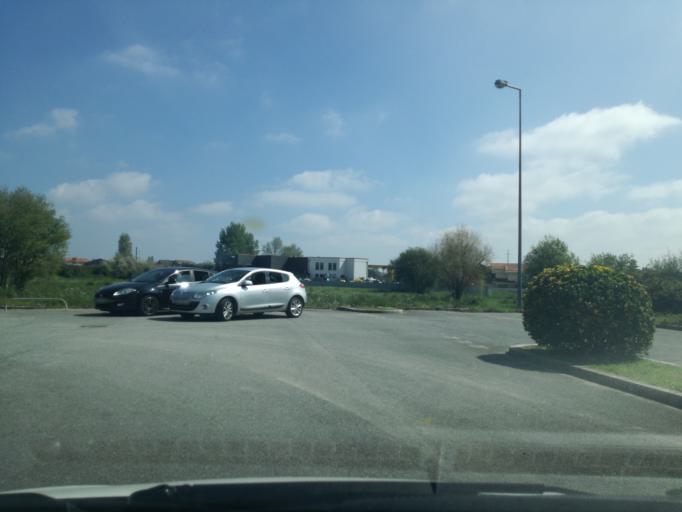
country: PT
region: Porto
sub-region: Matosinhos
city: Santa Cruz do Bispo
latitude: 41.2472
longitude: -8.6750
